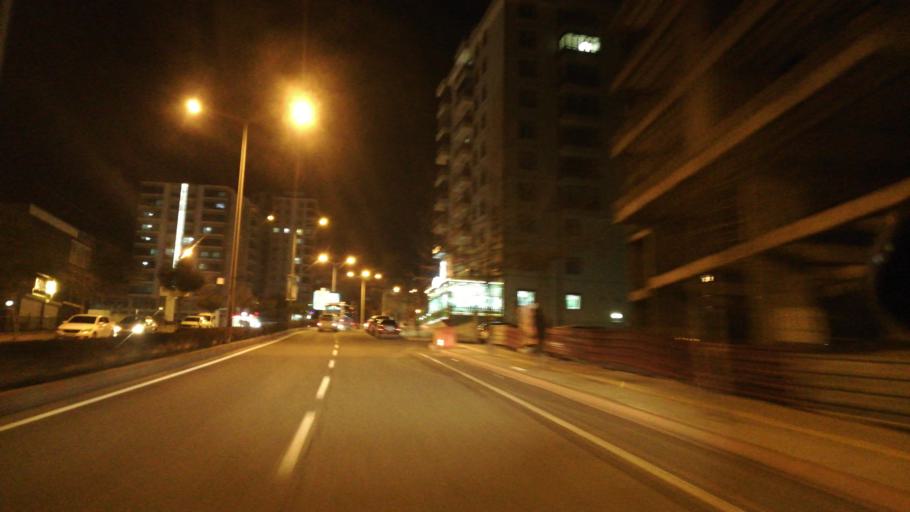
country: TR
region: Kahramanmaras
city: Kahramanmaras
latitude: 37.5921
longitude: 36.8593
